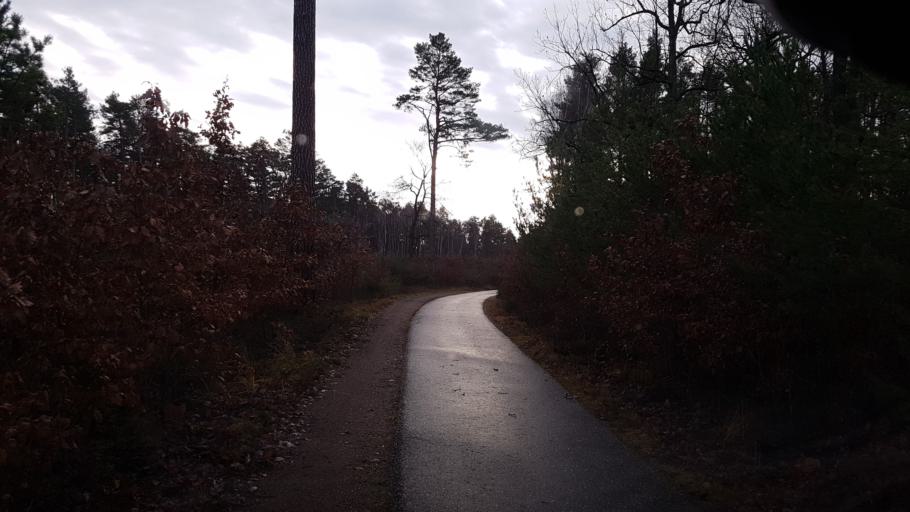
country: DE
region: Brandenburg
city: Lebusa
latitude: 51.7698
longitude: 13.4266
